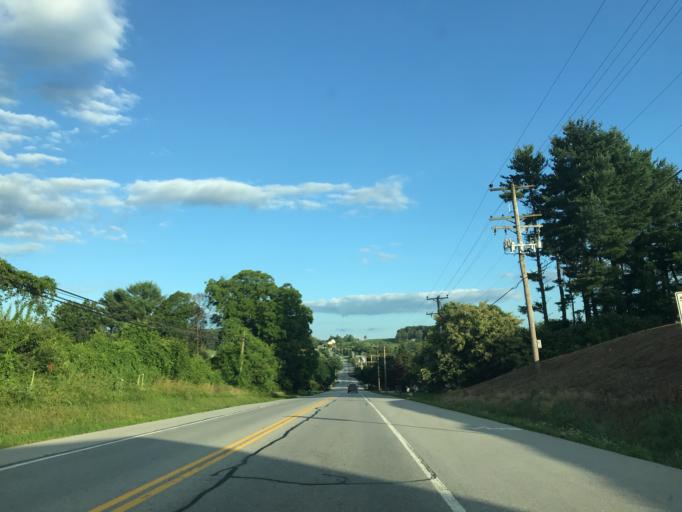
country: US
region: Maryland
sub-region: Carroll County
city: Manchester
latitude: 39.6941
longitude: -76.9014
